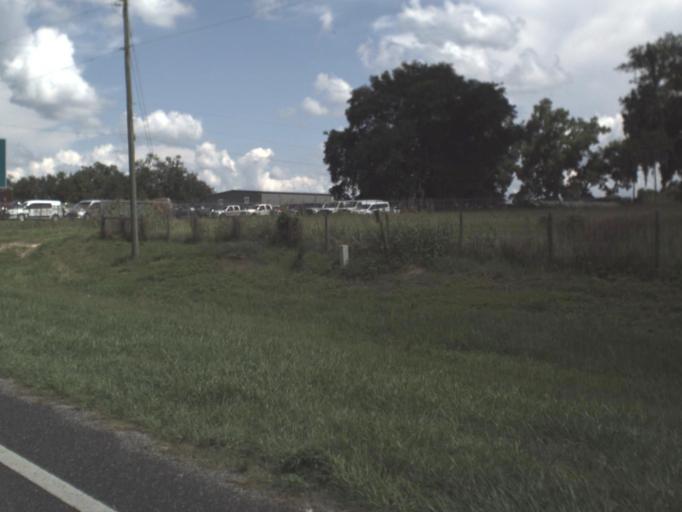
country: US
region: Florida
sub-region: Alachua County
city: High Springs
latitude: 29.8056
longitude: -82.5333
